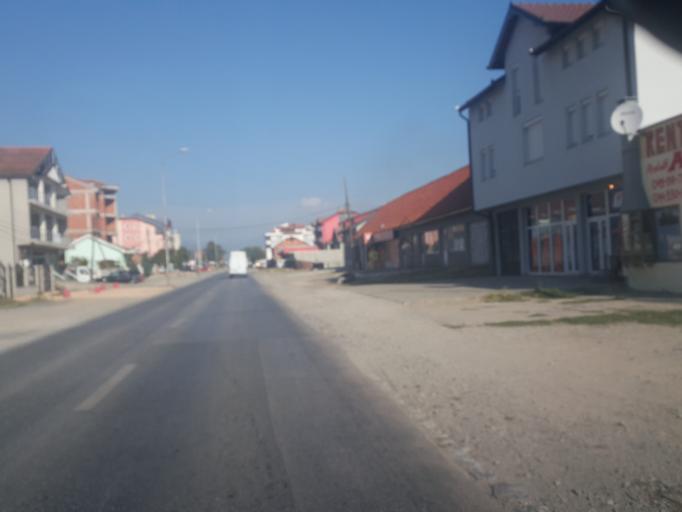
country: XK
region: Gjakova
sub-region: Komuna e Gjakoves
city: Gjakove
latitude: 42.4025
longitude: 20.4133
